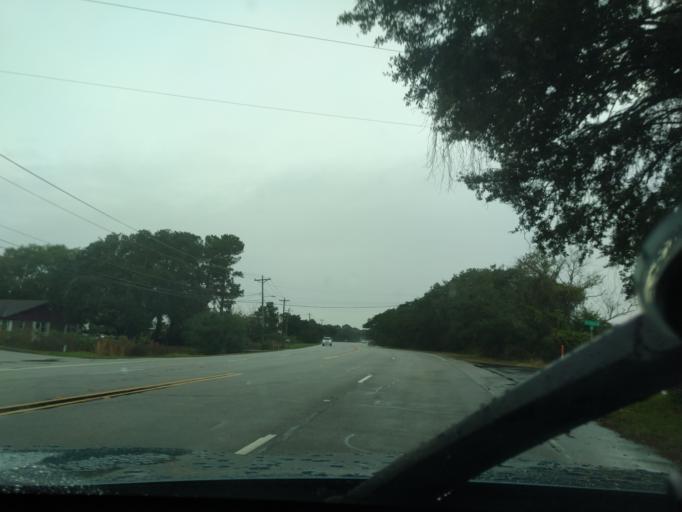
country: US
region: South Carolina
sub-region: Charleston County
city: Folly Beach
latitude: 32.6875
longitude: -79.9607
